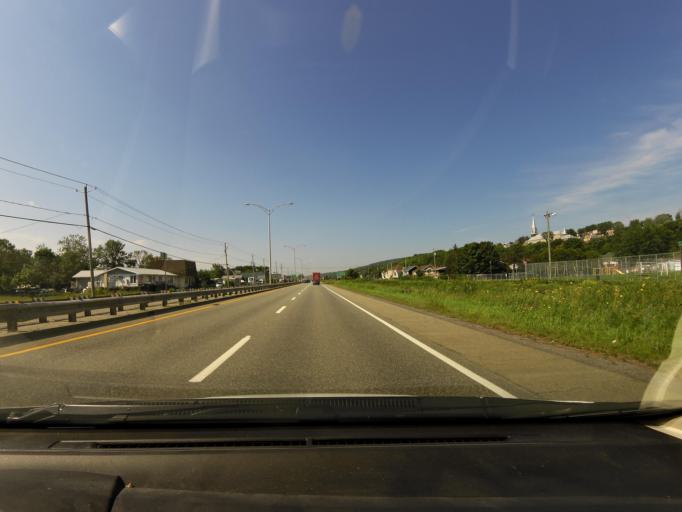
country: CA
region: Quebec
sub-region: Capitale-Nationale
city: Chateau-Richer
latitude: 46.9158
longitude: -71.0872
